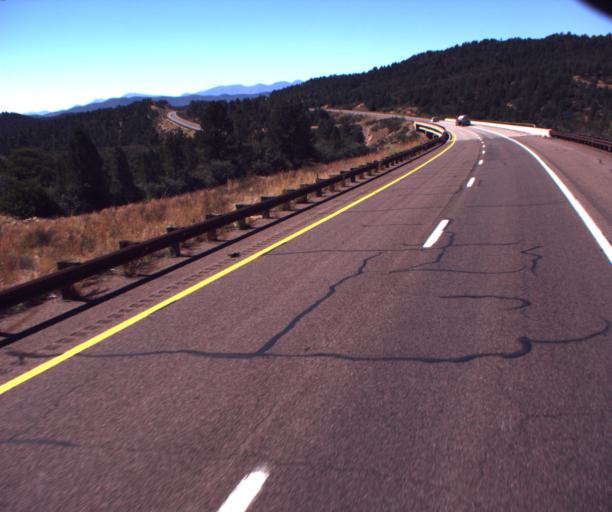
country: US
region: Arizona
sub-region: Gila County
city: Star Valley
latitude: 34.2788
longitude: -111.1676
